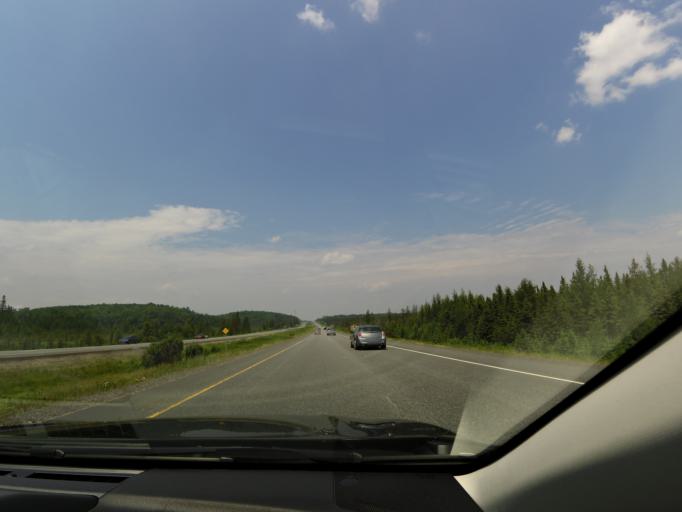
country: CA
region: Ontario
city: Huntsville
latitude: 45.4735
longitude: -79.2698
